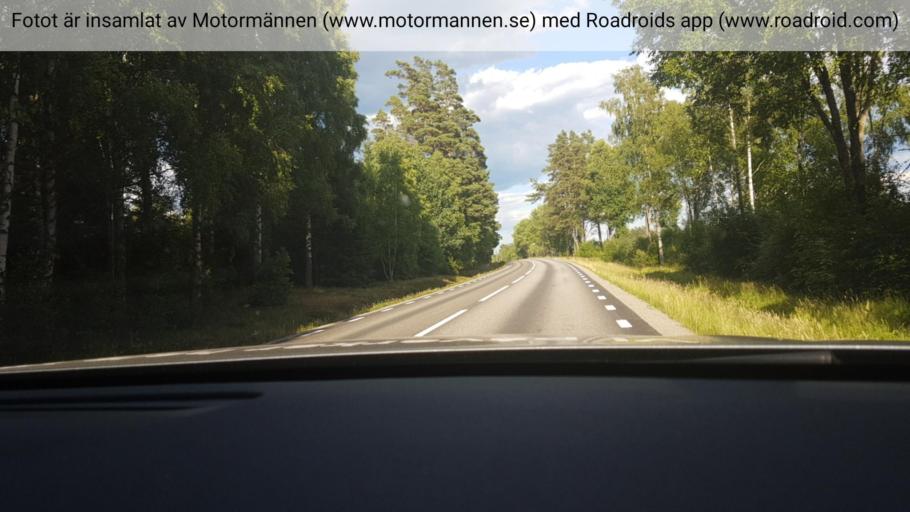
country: SE
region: Vaestra Goetaland
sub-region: Tranemo Kommun
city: Tranemo
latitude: 57.4774
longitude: 13.3053
